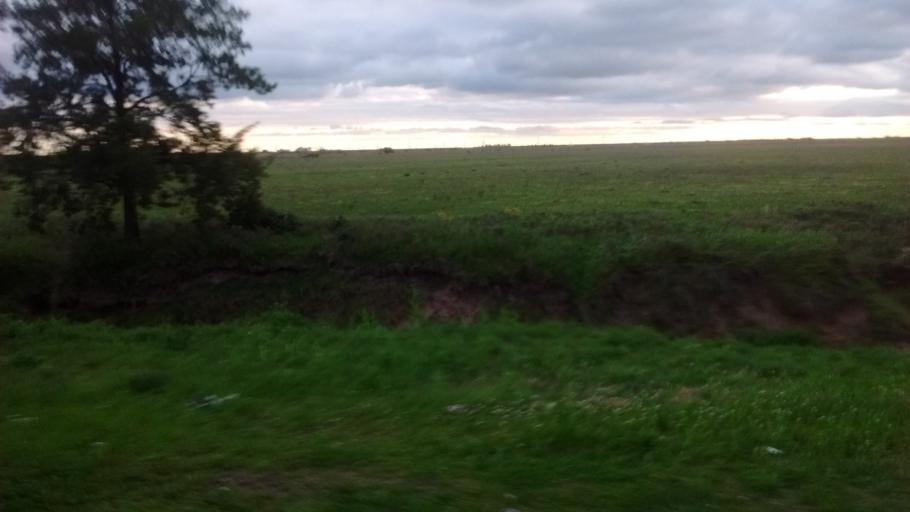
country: AR
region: Santa Fe
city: Funes
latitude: -32.9305
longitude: -60.7670
